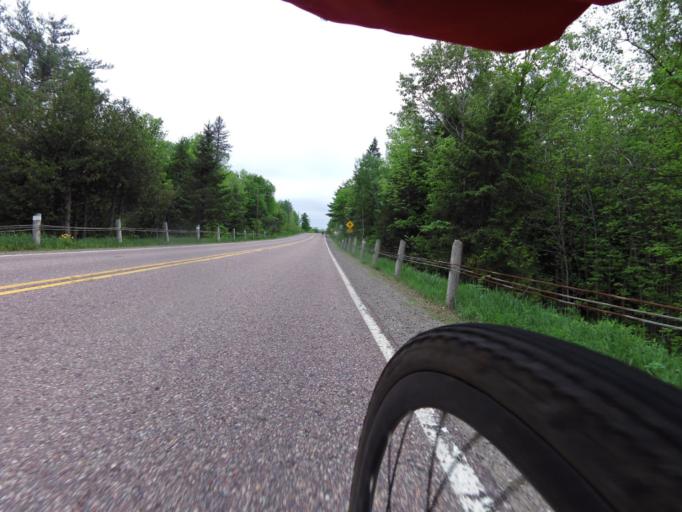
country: CA
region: Ontario
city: Renfrew
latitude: 45.2964
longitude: -76.7114
